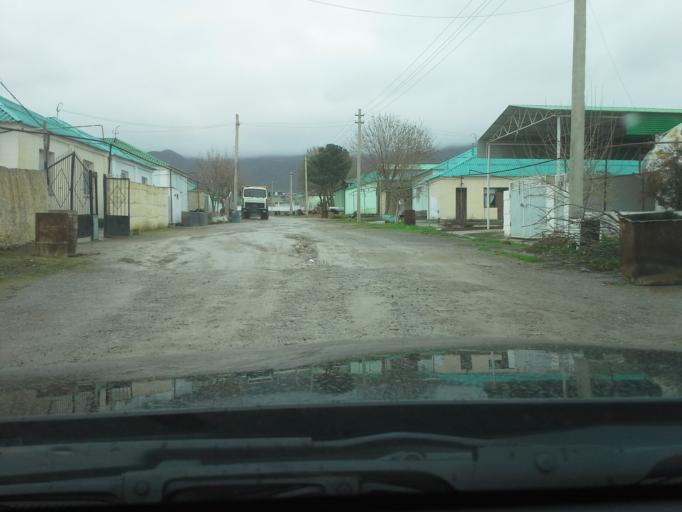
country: TM
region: Ahal
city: Abadan
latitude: 37.9660
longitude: 58.2087
